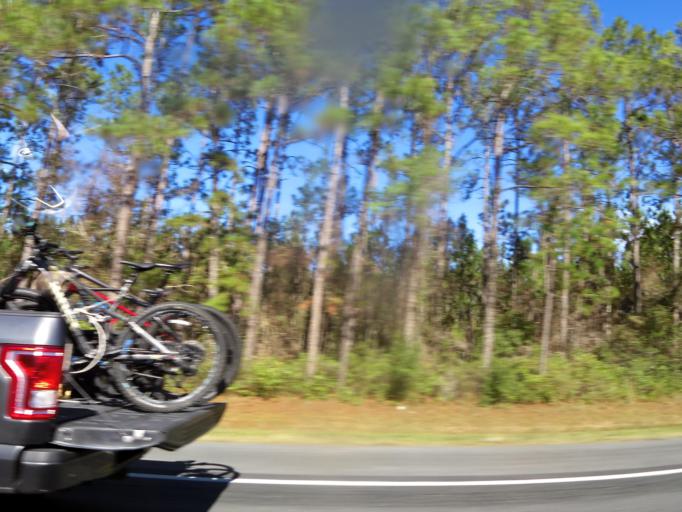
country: US
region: Florida
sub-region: Baker County
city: Macclenny
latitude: 30.2544
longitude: -82.3462
